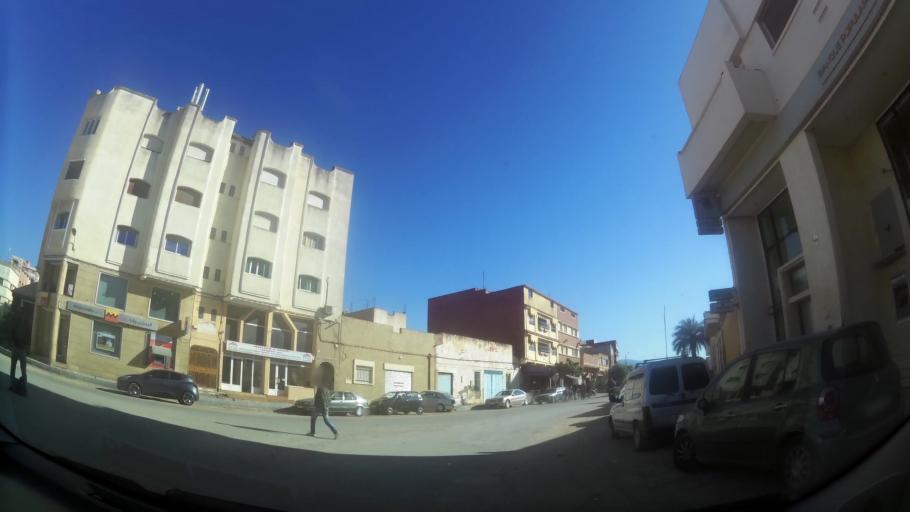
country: MA
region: Oriental
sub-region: Berkane-Taourirt
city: Ahfir
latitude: 34.9509
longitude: -2.1007
